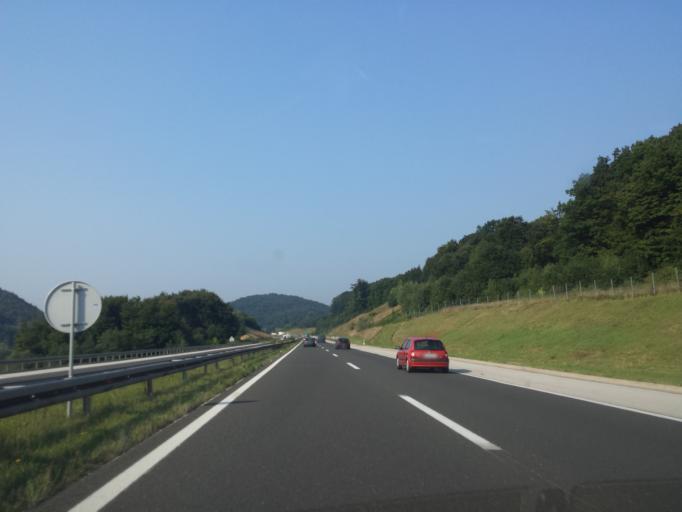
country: HR
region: Karlovacka
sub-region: Grad Karlovac
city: Karlovac
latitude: 45.5016
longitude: 15.4552
